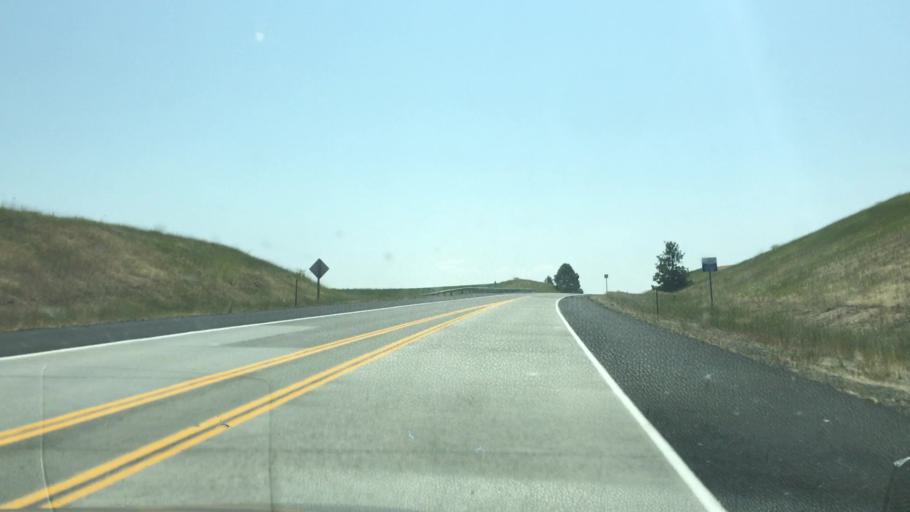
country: US
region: Idaho
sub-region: Lewis County
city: Nezperce
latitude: 46.0978
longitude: -116.3504
